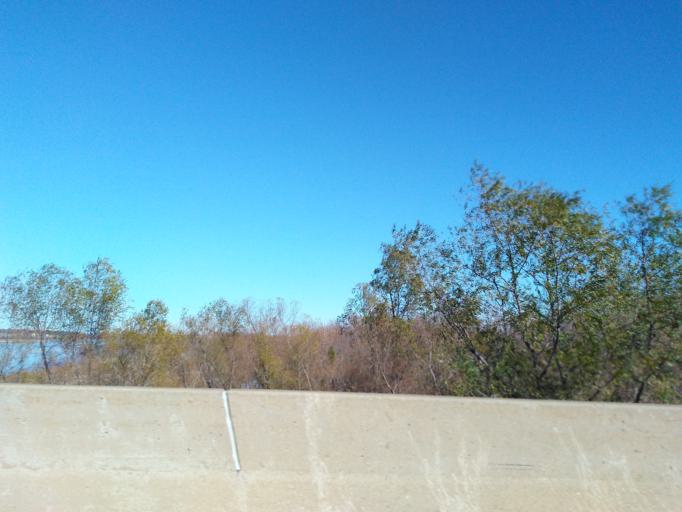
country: US
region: Missouri
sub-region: Saint Louis County
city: Oakville
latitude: 38.4853
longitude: -90.2701
